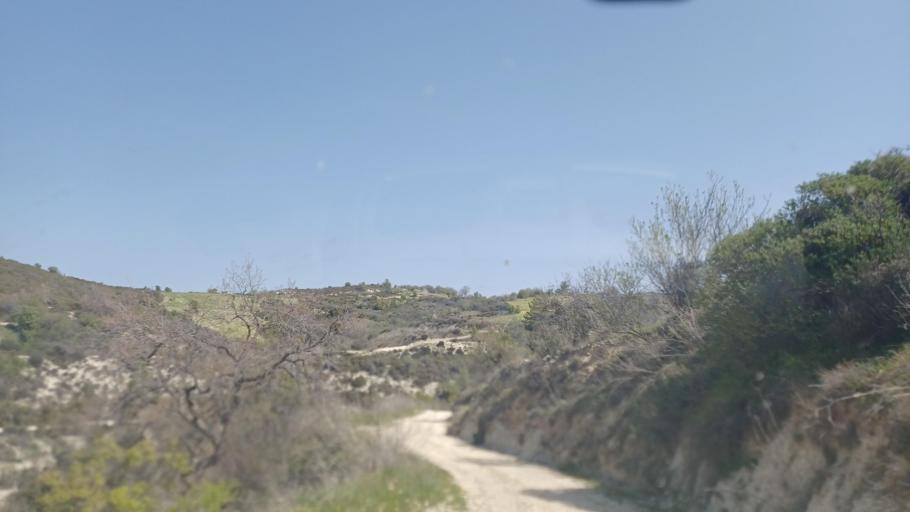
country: CY
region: Limassol
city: Pachna
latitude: 34.8580
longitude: 32.7427
